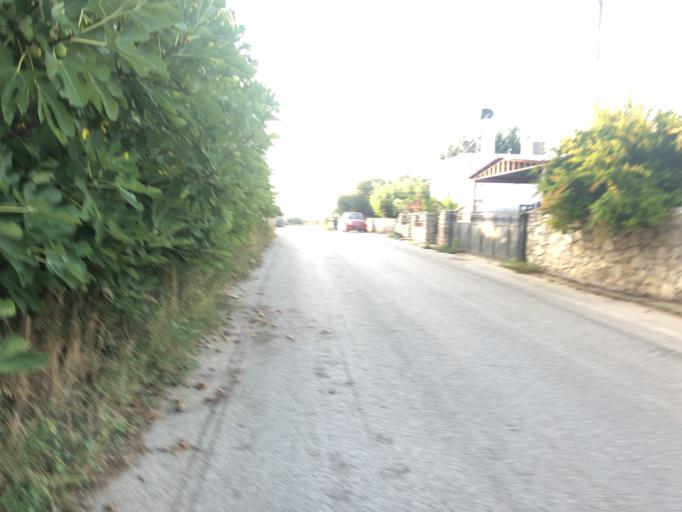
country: GR
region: Crete
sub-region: Nomos Chanias
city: Georgioupolis
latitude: 35.3487
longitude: 24.2846
